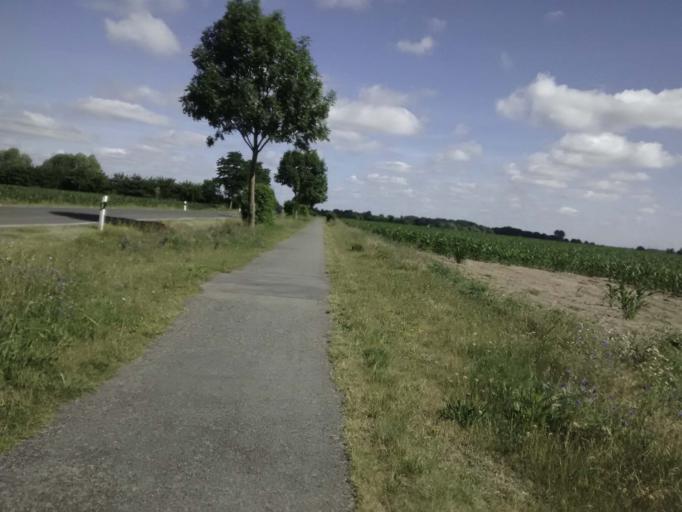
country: DE
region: Saxony-Anhalt
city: Jerichow
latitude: 52.4246
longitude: 11.9639
